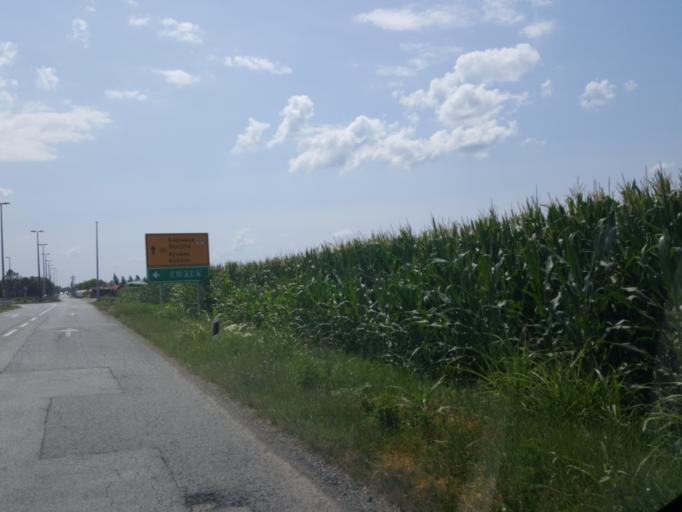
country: RS
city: Ravnje
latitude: 45.0354
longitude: 19.3847
